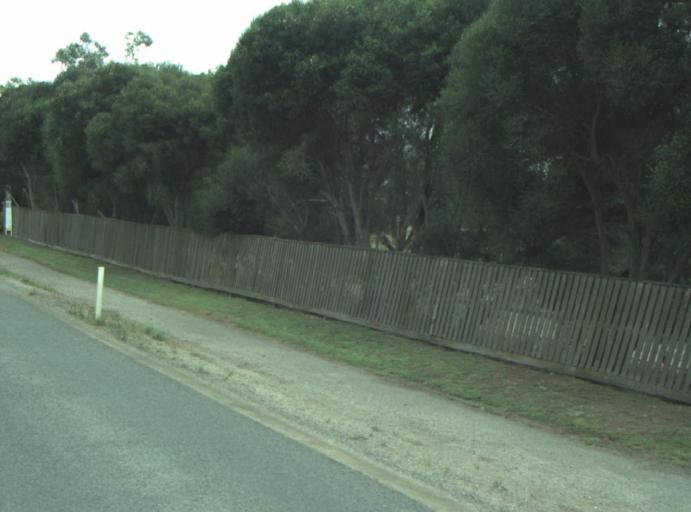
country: AU
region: Victoria
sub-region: Greater Geelong
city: Bell Post Hill
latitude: -38.0750
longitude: 144.3321
